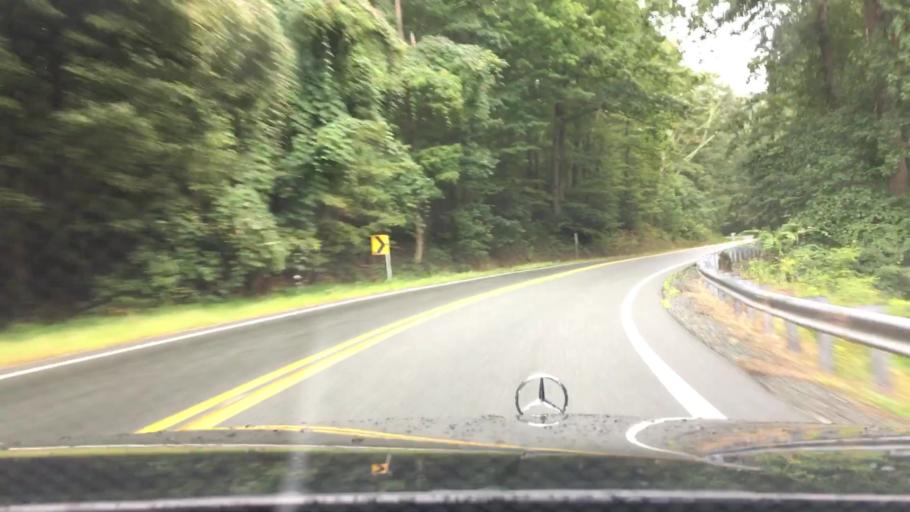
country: US
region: Virginia
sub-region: Nelson County
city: Nellysford
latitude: 37.8607
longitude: -78.9199
